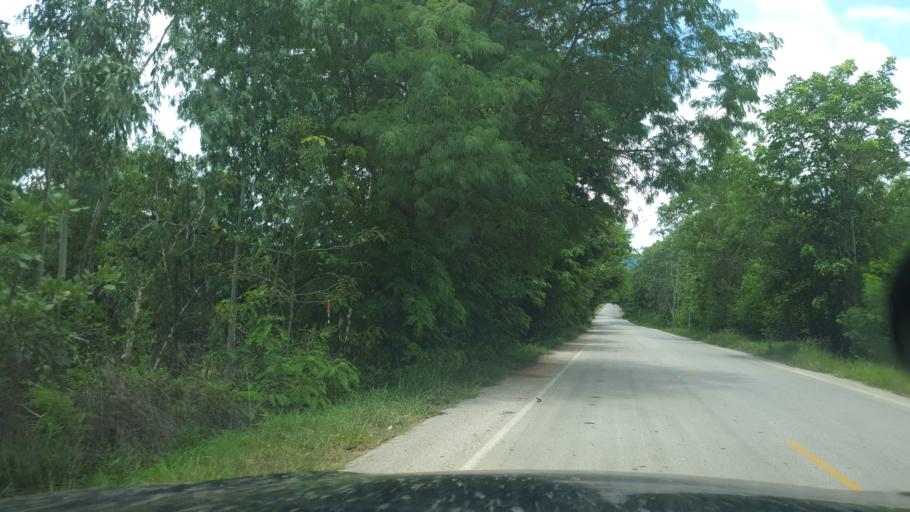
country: TH
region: Lampang
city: Sop Prap
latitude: 17.9262
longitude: 99.3788
